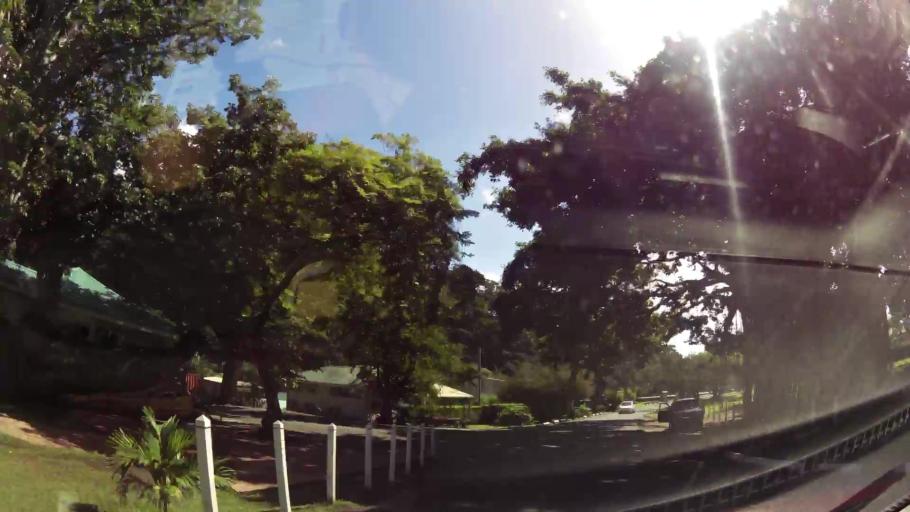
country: DM
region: Saint George
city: Roseau
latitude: 15.2982
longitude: -61.3827
